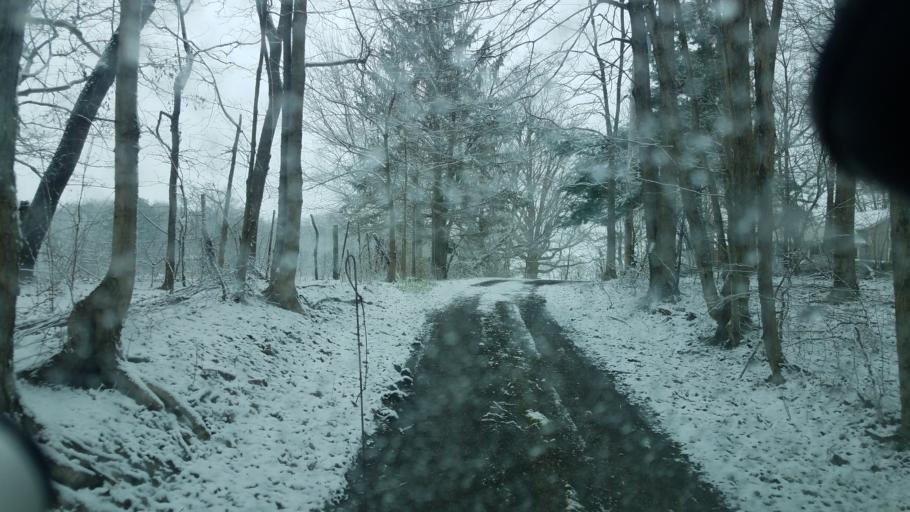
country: US
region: Ohio
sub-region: Crawford County
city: Crestline
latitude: 40.7260
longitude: -82.7190
